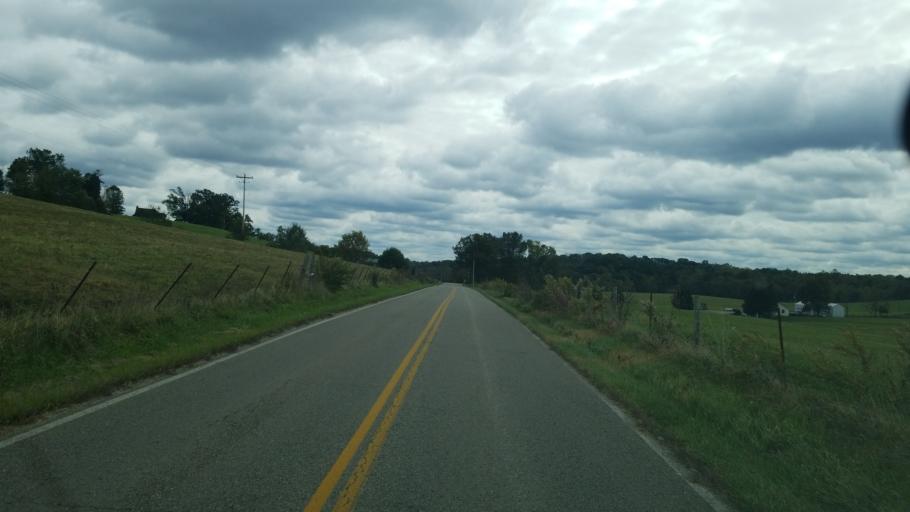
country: US
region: Ohio
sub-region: Jackson County
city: Jackson
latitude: 39.1366
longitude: -82.6486
